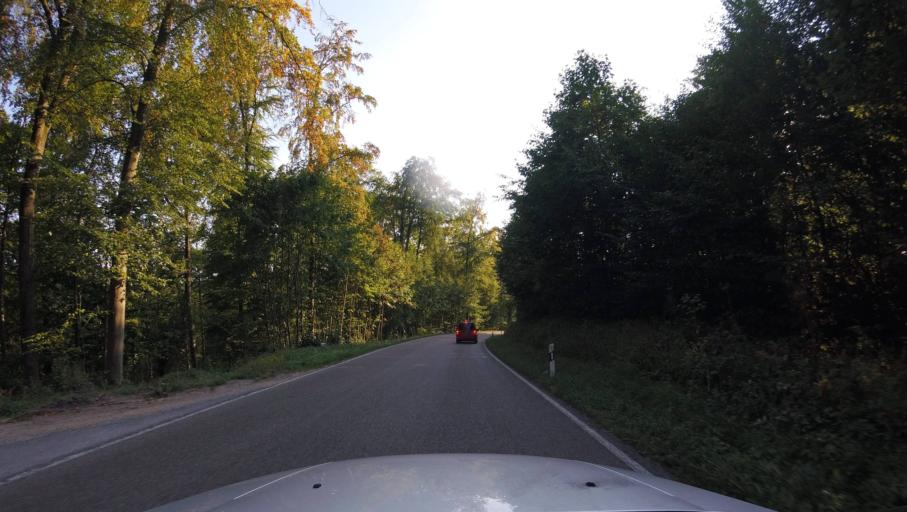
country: DE
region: Baden-Wuerttemberg
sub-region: Regierungsbezirk Stuttgart
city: Allmersbach im Tal
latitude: 48.8952
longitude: 9.4440
